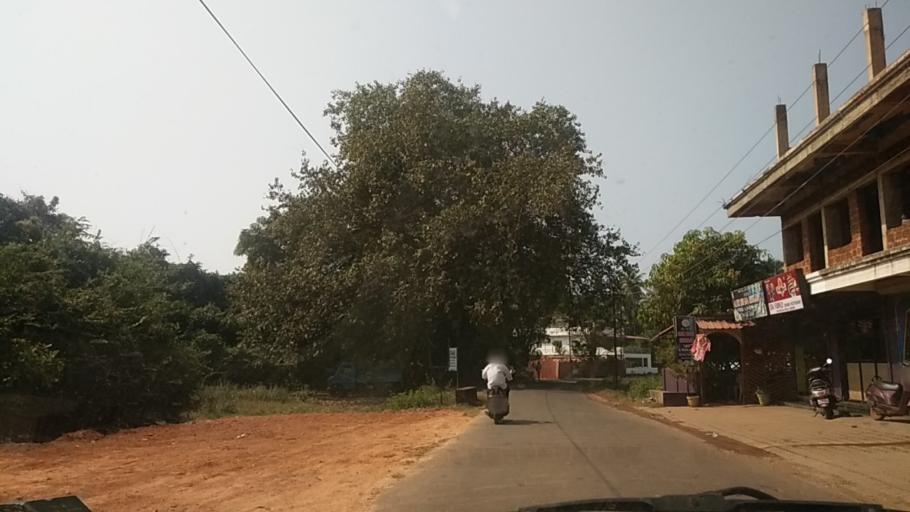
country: IN
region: Goa
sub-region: South Goa
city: Kankon
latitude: 15.0107
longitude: 74.0302
